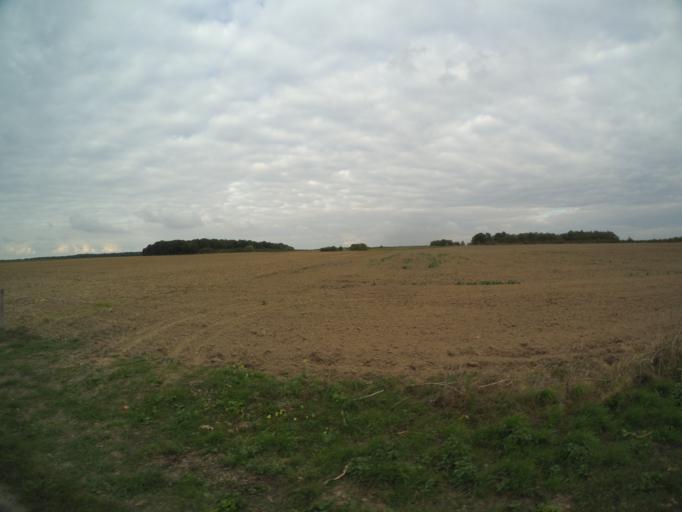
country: FR
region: Centre
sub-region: Departement d'Indre-et-Loire
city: Auzouer-en-Touraine
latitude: 47.4980
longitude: 0.9625
